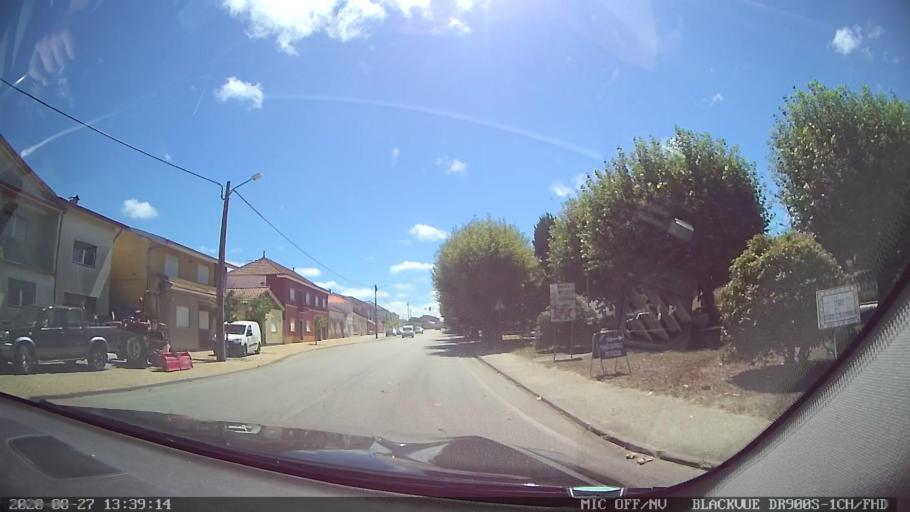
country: PT
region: Coimbra
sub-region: Mira
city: Mira
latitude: 40.4429
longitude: -8.7301
